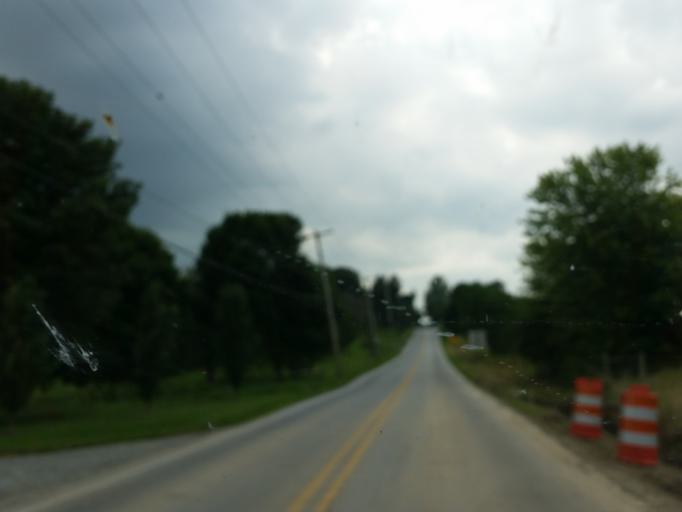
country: US
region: Pennsylvania
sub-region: Chester County
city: Oxford
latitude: 39.8404
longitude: -75.9371
